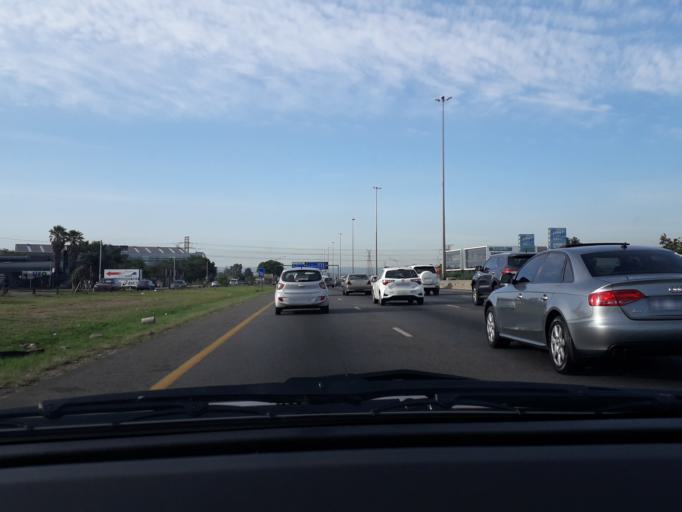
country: ZA
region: Gauteng
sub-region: City of Johannesburg Metropolitan Municipality
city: Modderfontein
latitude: -26.0856
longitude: 28.0865
